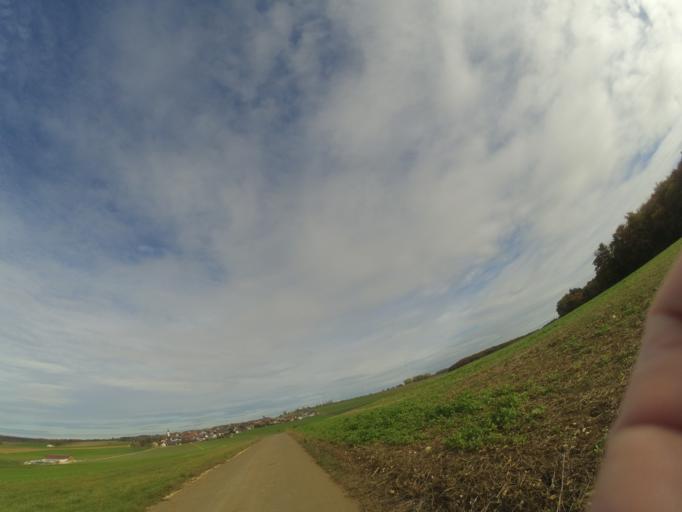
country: DE
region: Baden-Wuerttemberg
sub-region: Tuebingen Region
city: Lonsee
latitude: 48.5539
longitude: 9.9271
